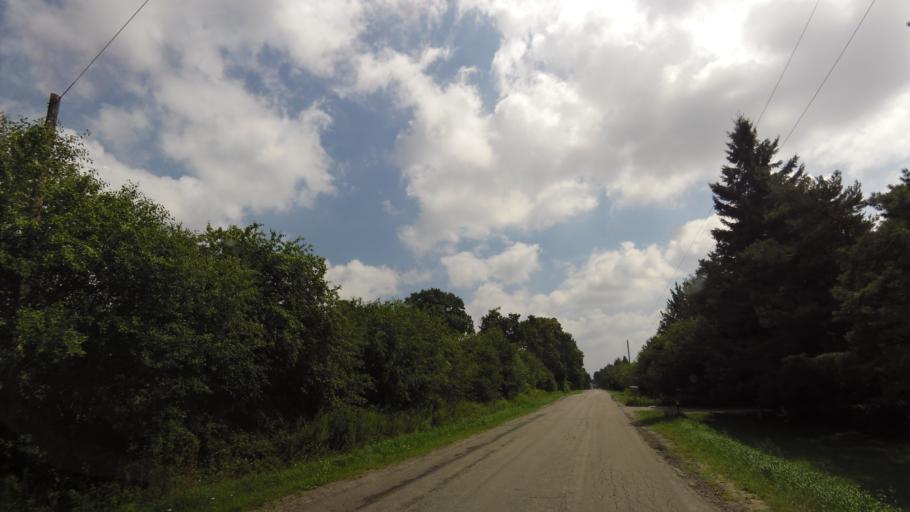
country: CA
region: Ontario
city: Oshawa
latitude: 43.9955
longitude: -78.8740
